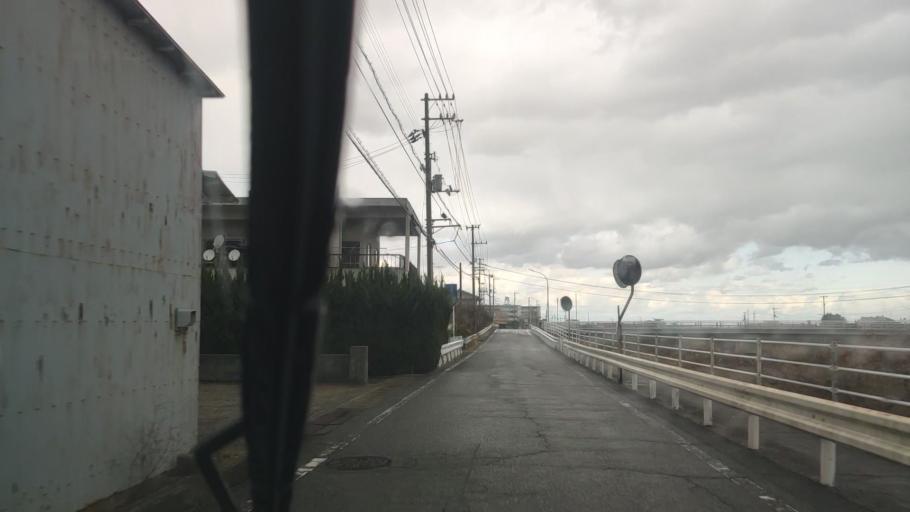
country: JP
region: Tokushima
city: Ishii
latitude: 34.2138
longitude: 134.4060
